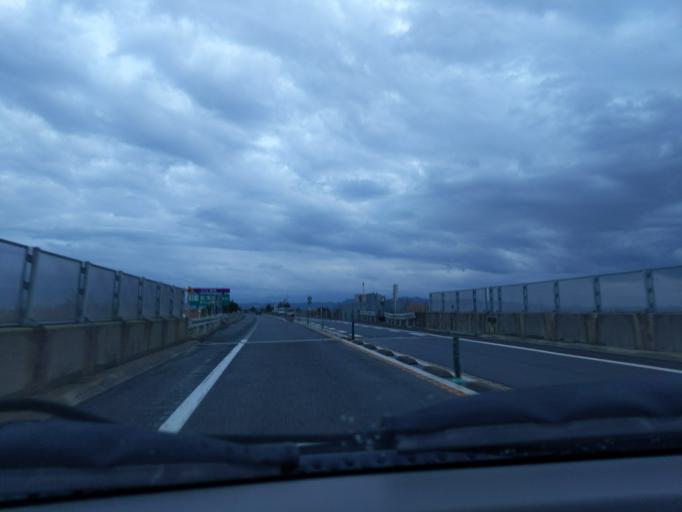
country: JP
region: Niigata
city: Kameda-honcho
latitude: 37.8324
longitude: 139.0724
